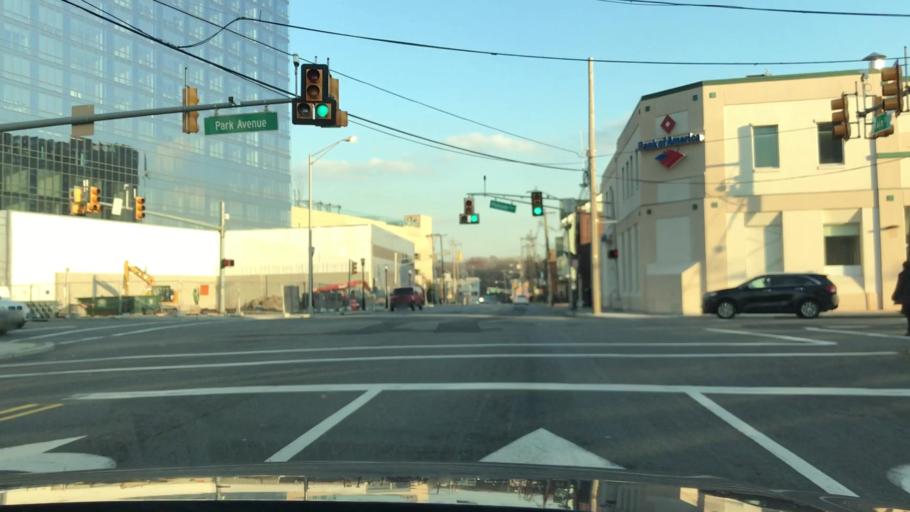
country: US
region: New Jersey
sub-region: Bergen County
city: Fort Lee
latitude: 40.8510
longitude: -73.9687
